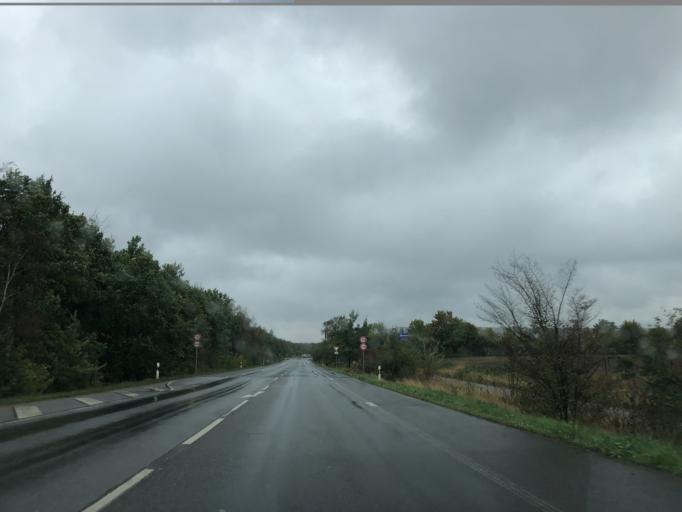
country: DE
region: North Rhine-Westphalia
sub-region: Regierungsbezirk Koln
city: Bedburg
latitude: 51.0169
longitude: 6.5814
